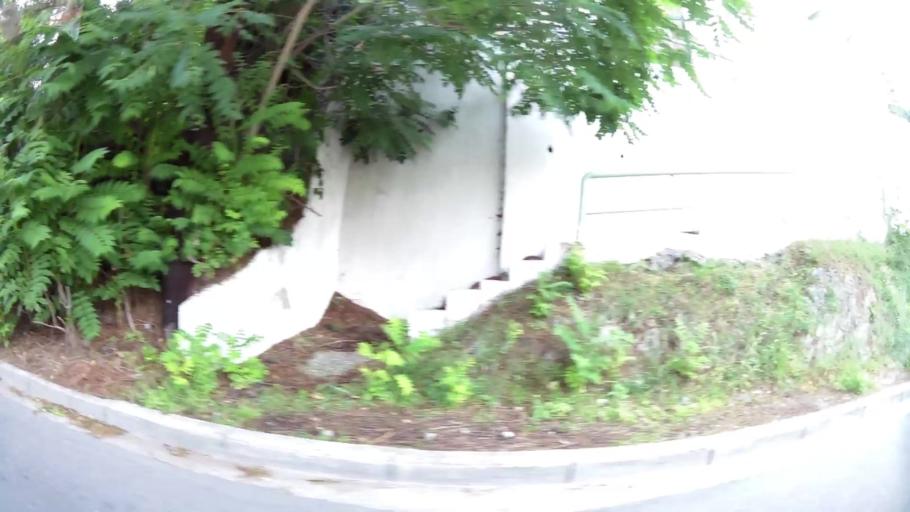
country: GR
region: Central Macedonia
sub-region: Nomos Thessalonikis
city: Panorama
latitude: 40.5910
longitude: 23.0279
